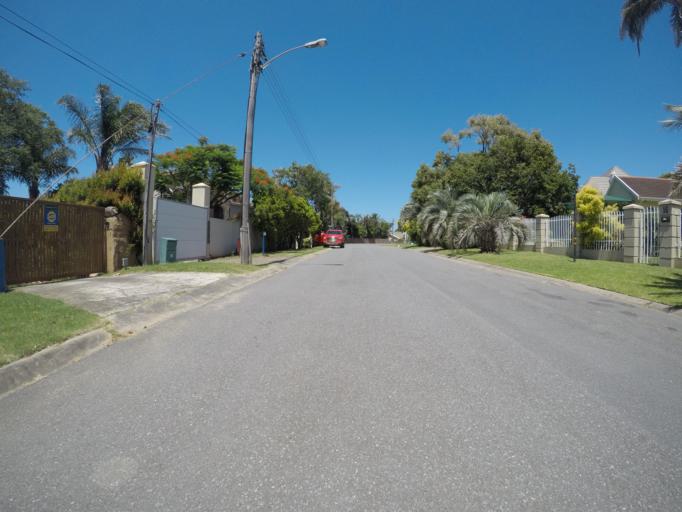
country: ZA
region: Eastern Cape
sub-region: Buffalo City Metropolitan Municipality
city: East London
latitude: -32.9659
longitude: 27.9550
